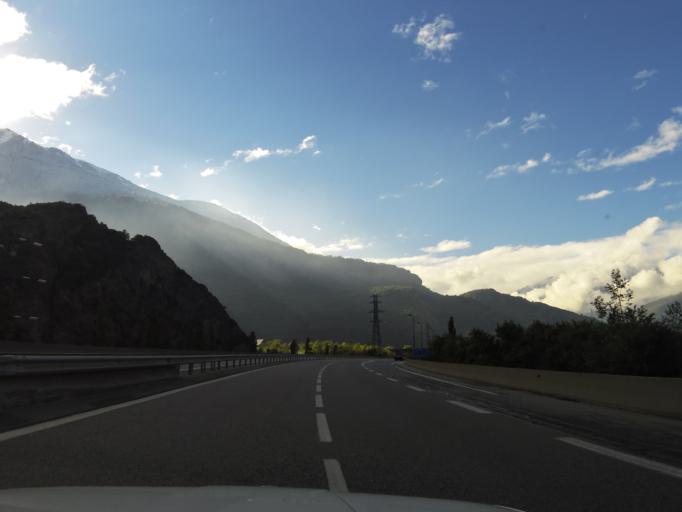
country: FR
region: Rhone-Alpes
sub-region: Departement de la Savoie
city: Saint-Jean-de-Maurienne
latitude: 45.3016
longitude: 6.3531
